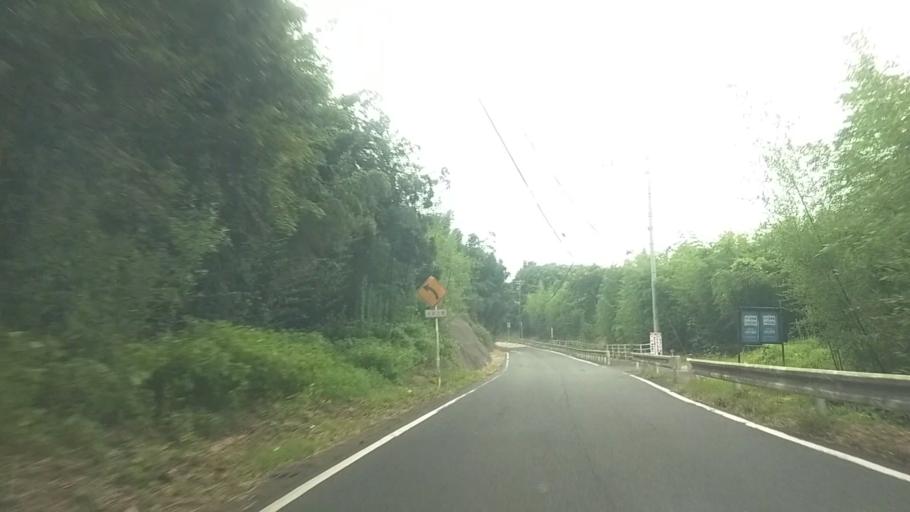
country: JP
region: Chiba
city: Kimitsu
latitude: 35.2379
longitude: 140.0011
